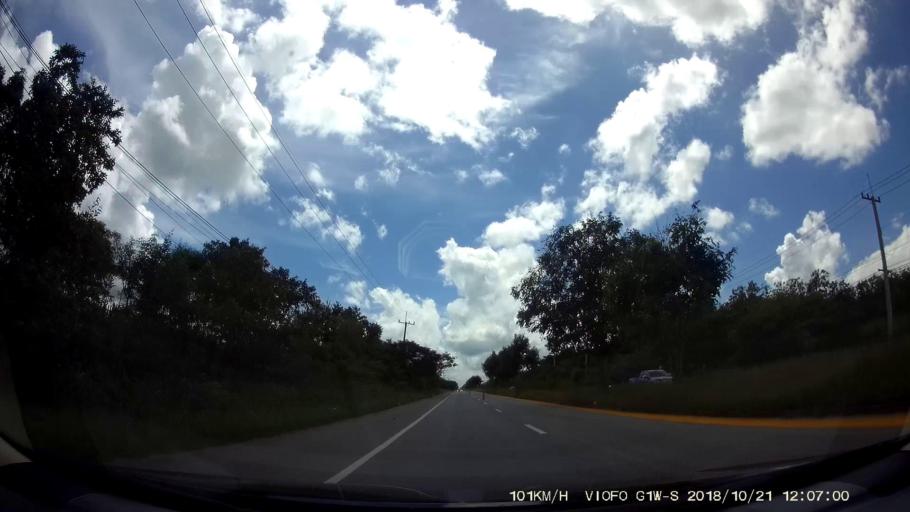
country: TH
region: Chaiyaphum
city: Chatturat
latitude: 15.4544
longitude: 101.8274
